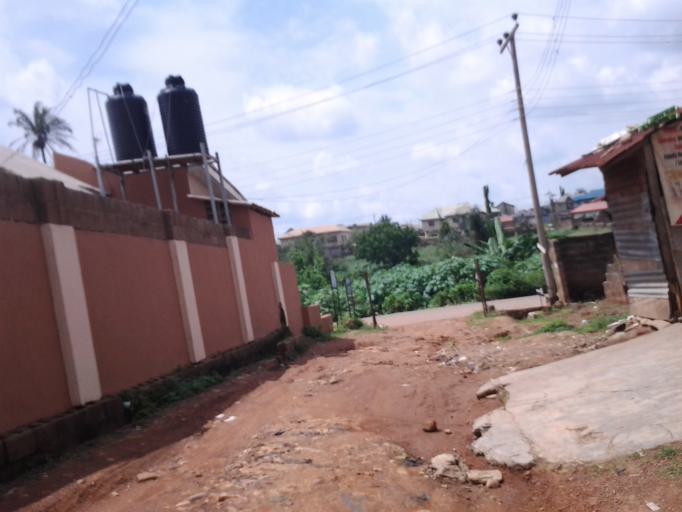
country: NG
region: Oyo
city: Ibadan
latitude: 7.4361
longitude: 3.9533
